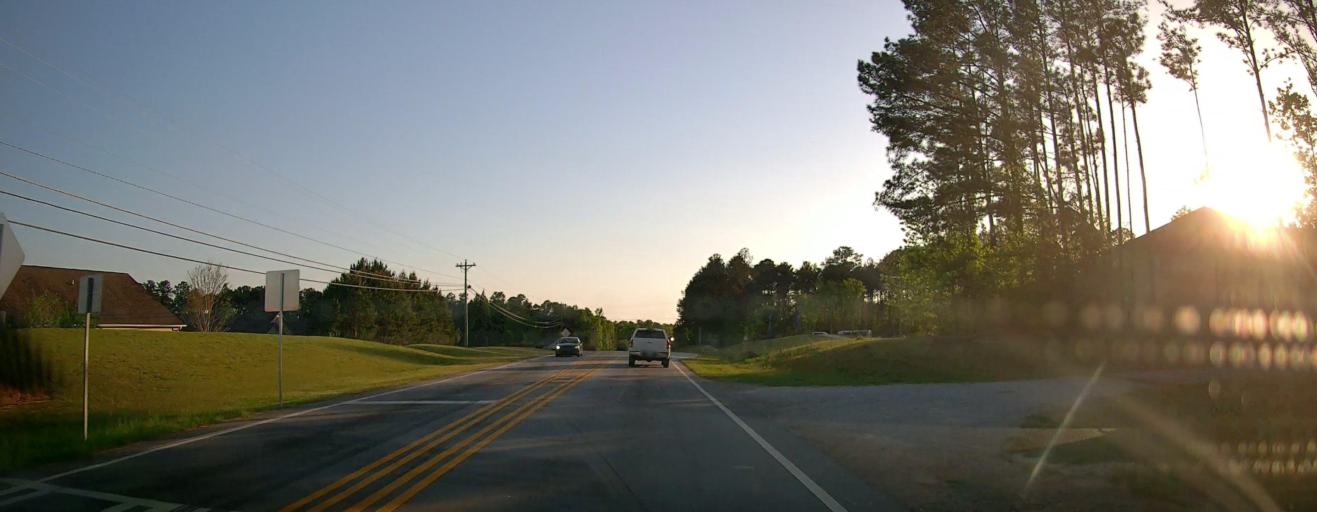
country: US
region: Georgia
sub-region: Newton County
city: Covington
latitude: 33.5746
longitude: -83.8402
